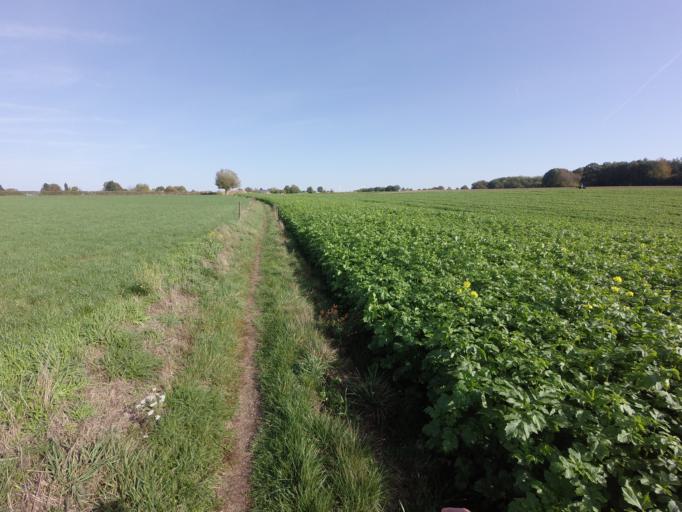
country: NL
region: Limburg
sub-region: Gemeente Simpelveld
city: Simpelveld
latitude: 50.8156
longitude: 5.9703
